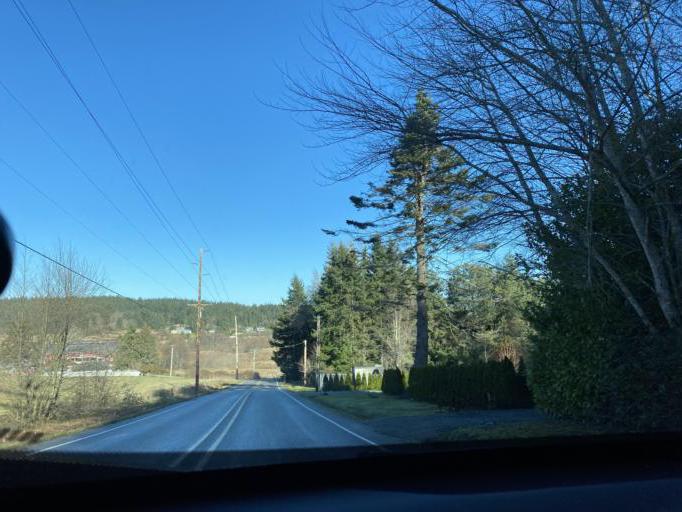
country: US
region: Washington
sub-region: Island County
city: Camano
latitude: 48.1039
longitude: -122.5741
